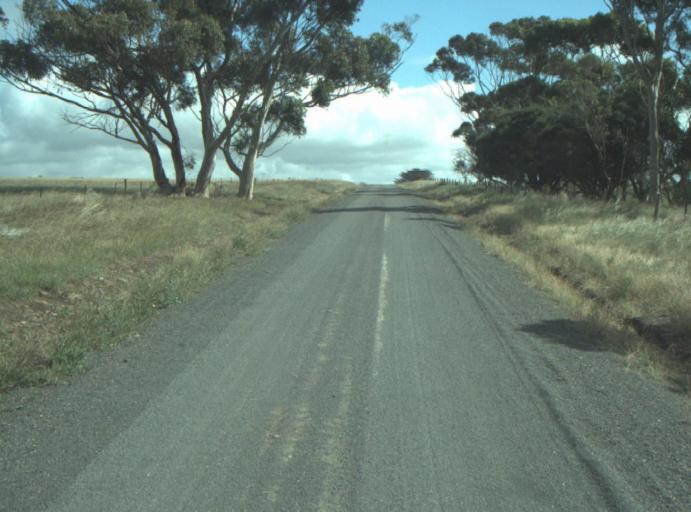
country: AU
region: Victoria
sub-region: Greater Geelong
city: Lara
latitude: -37.8982
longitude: 144.3180
